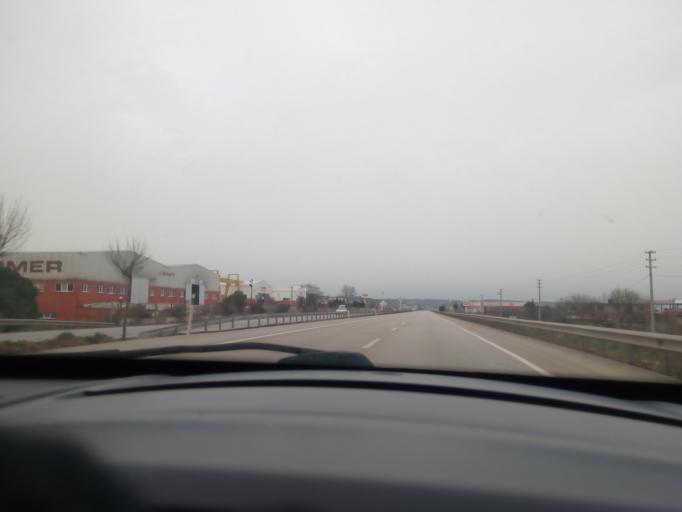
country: TR
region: Bursa
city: Tatkavakli
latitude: 40.0294
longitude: 28.3083
